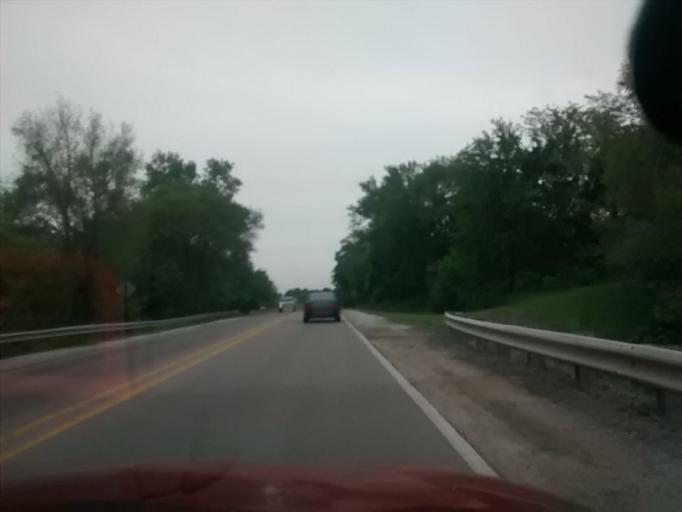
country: US
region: Nebraska
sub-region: Sarpy County
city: Offutt Air Force Base
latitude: 41.1517
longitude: -95.9668
